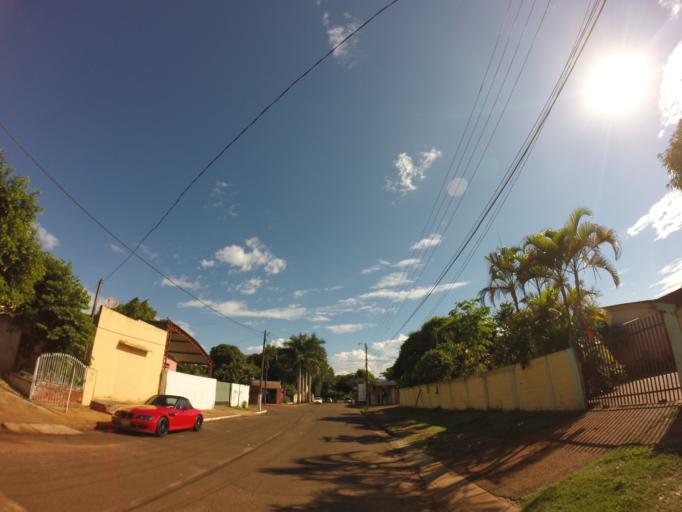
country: PY
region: Alto Parana
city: Ciudad del Este
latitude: -25.4078
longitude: -54.6269
